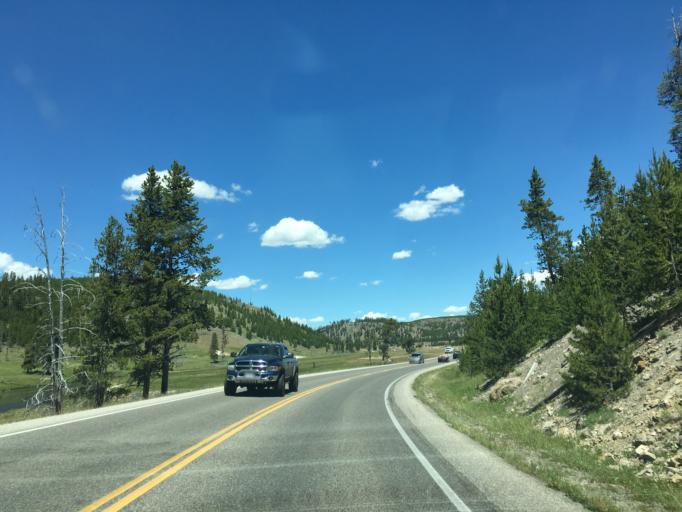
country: US
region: Montana
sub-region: Gallatin County
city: West Yellowstone
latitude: 44.5105
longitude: -110.8342
